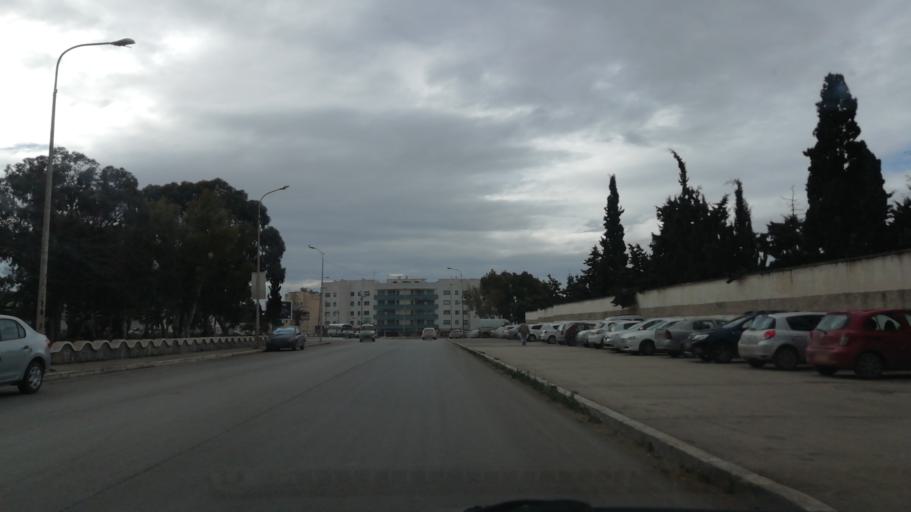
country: DZ
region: Oran
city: Oran
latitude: 35.6985
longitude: -0.6134
